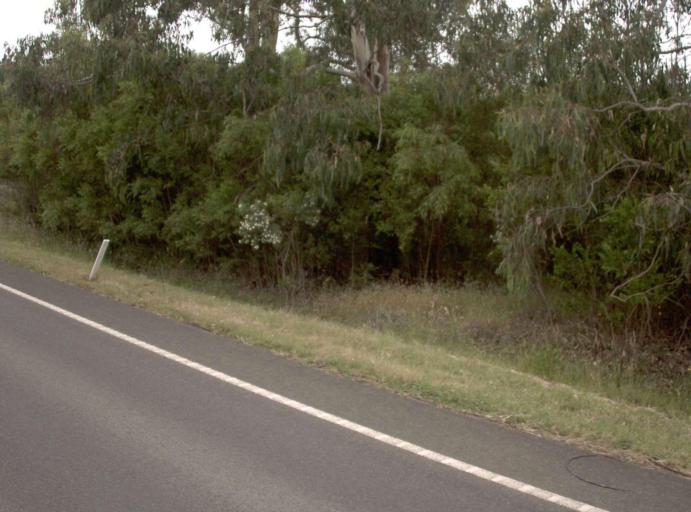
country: AU
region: Victoria
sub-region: Latrobe
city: Moe
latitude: -38.2953
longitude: 146.2886
